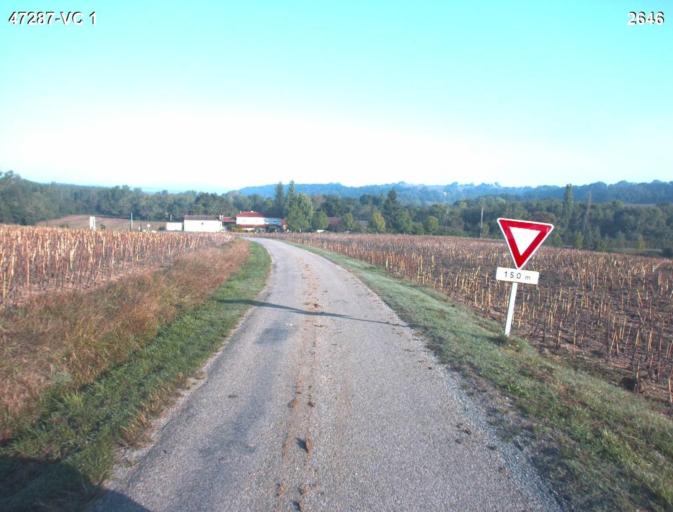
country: FR
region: Aquitaine
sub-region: Departement du Lot-et-Garonne
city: Sainte-Colombe-en-Bruilhois
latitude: 44.1436
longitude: 0.4435
